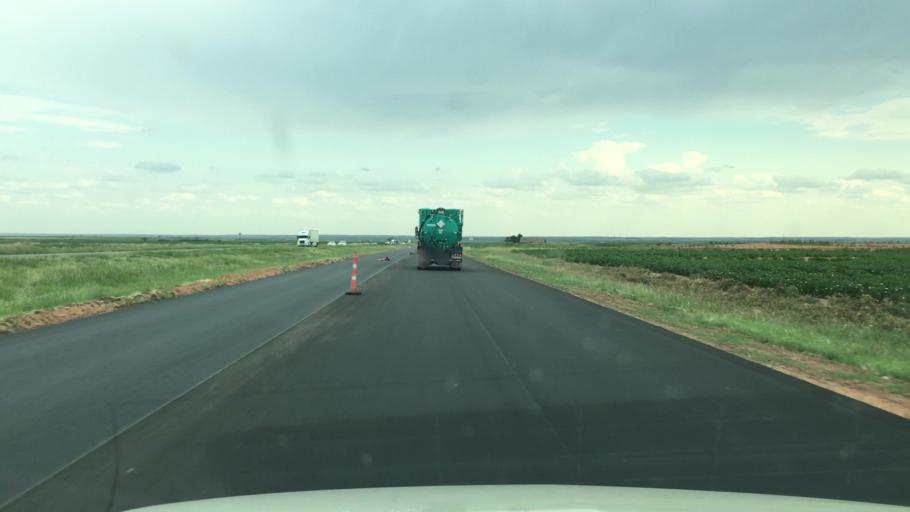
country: US
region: Texas
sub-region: Hall County
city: Memphis
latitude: 34.6247
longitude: -100.4738
